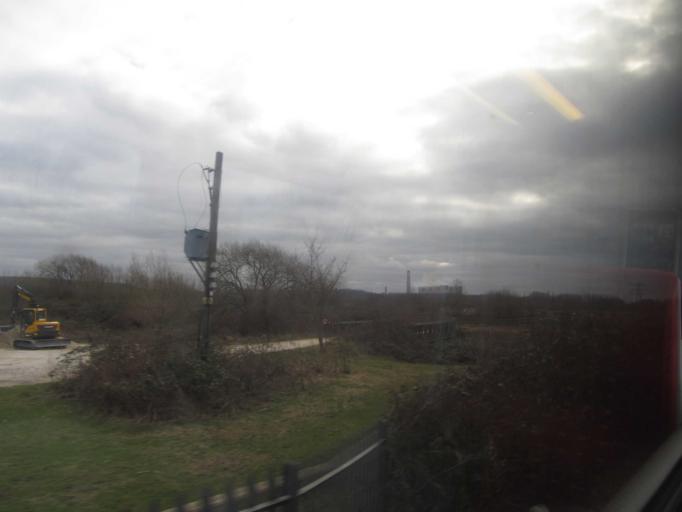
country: GB
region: England
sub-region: Derbyshire
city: Long Eaton
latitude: 52.8980
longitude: -1.2451
